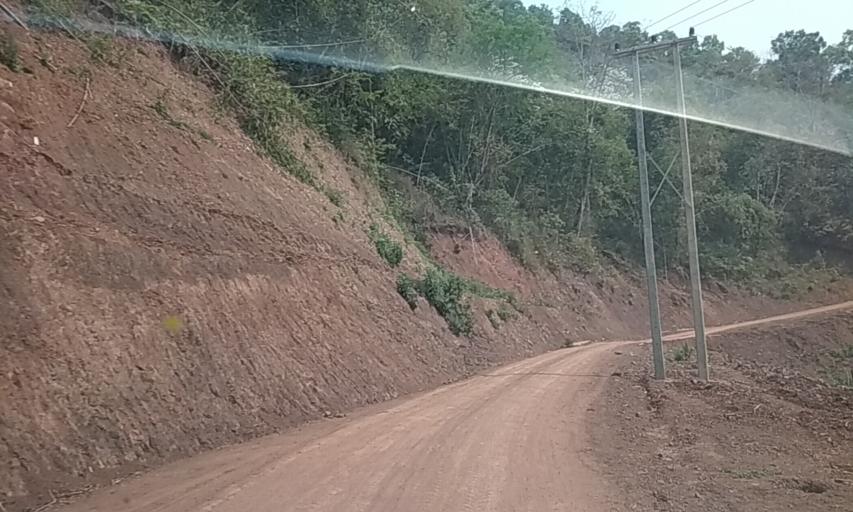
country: VN
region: Huyen Dien Bien
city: Dien Bien Phu
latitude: 21.4562
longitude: 102.7675
